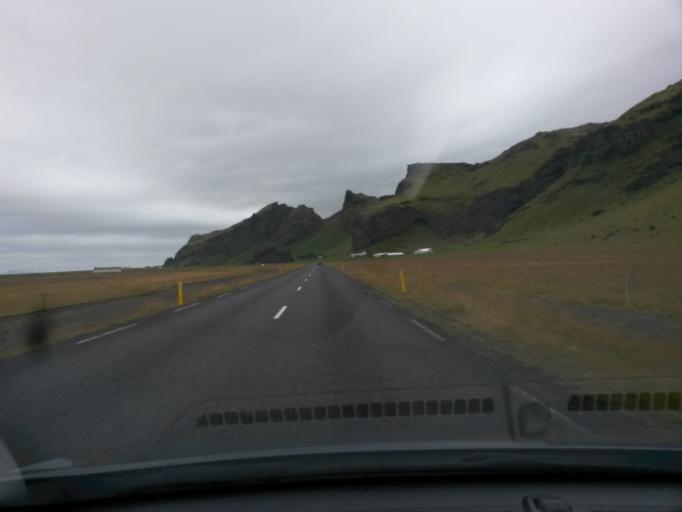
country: IS
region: South
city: Vestmannaeyjar
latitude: 63.5227
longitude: -19.5344
